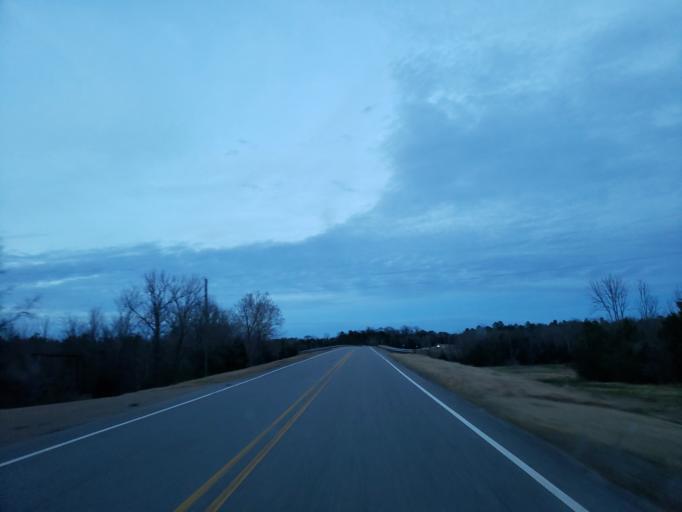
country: US
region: Alabama
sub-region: Greene County
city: Eutaw
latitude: 32.8563
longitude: -88.1010
